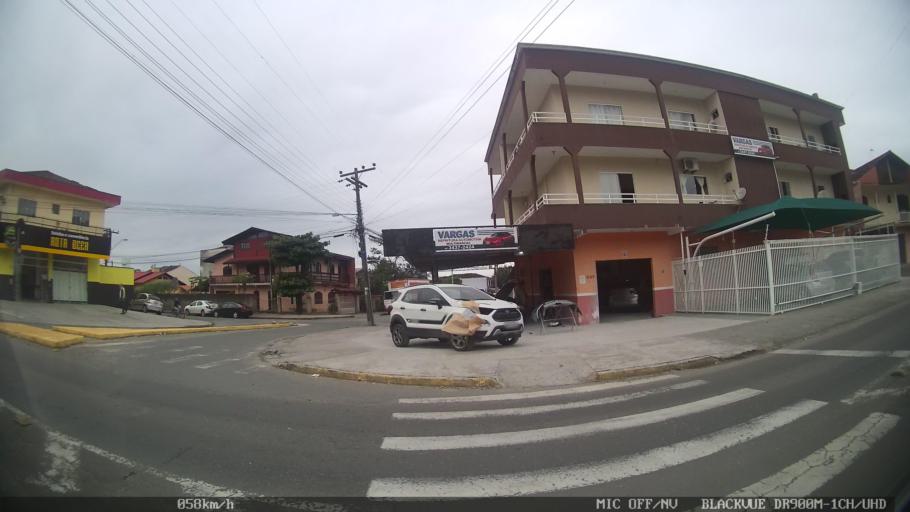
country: BR
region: Santa Catarina
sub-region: Joinville
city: Joinville
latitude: -26.2639
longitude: -48.8191
